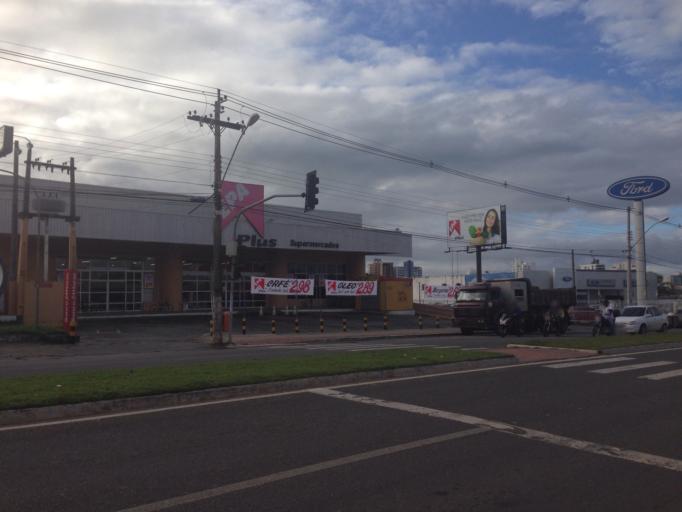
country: BR
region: Espirito Santo
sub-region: Guarapari
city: Guarapari
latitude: -20.6569
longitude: -40.5029
